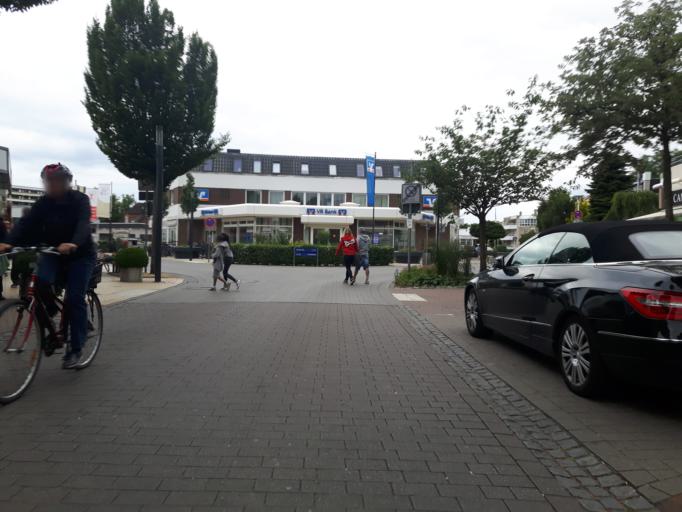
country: DE
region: Schleswig-Holstein
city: Gromitz
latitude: 54.1477
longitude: 10.9610
